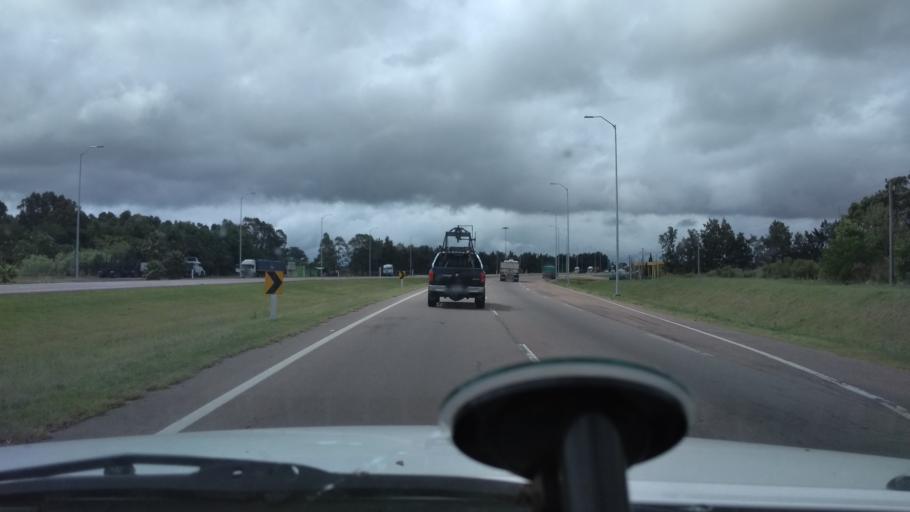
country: UY
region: Canelones
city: La Paz
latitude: -34.7835
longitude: -56.2748
